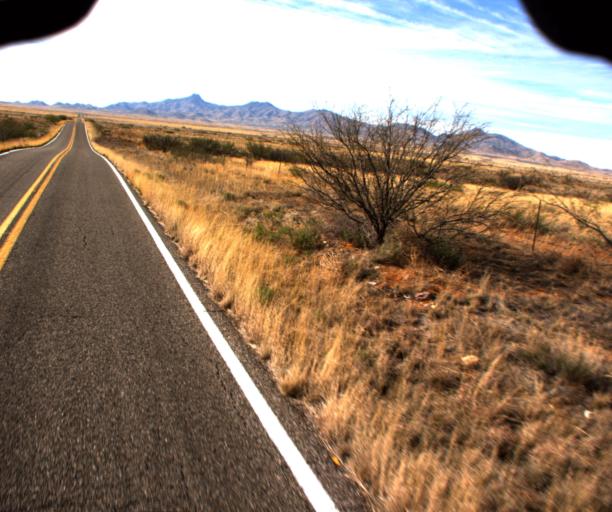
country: US
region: Arizona
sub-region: Cochise County
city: Willcox
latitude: 32.0560
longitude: -109.4969
